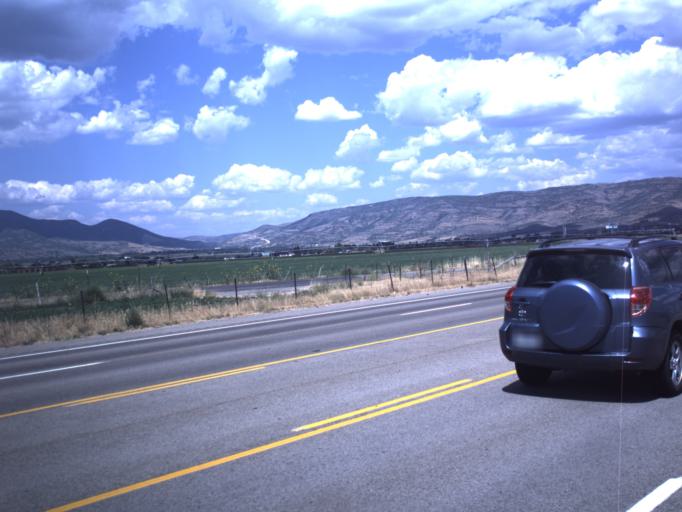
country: US
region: Utah
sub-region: Wasatch County
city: Heber
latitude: 40.4783
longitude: -111.4360
